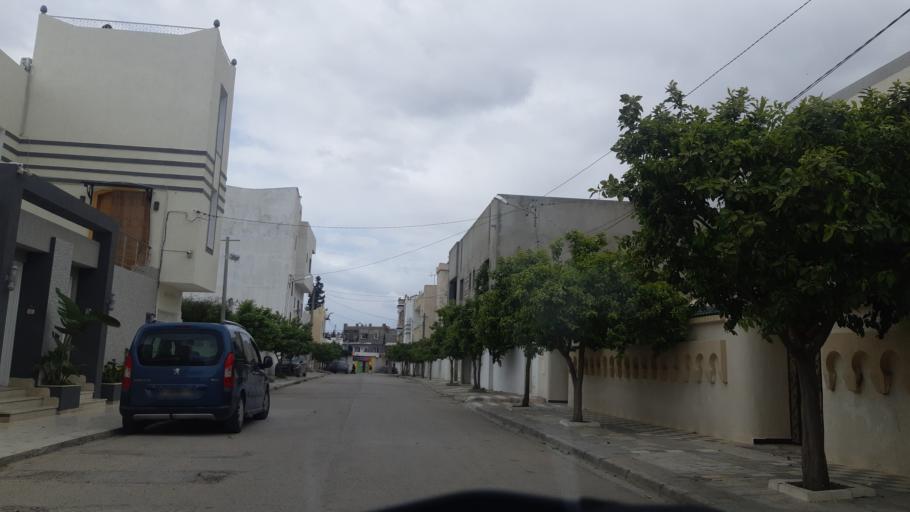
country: TN
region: Susah
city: Akouda
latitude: 35.8682
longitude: 10.5479
